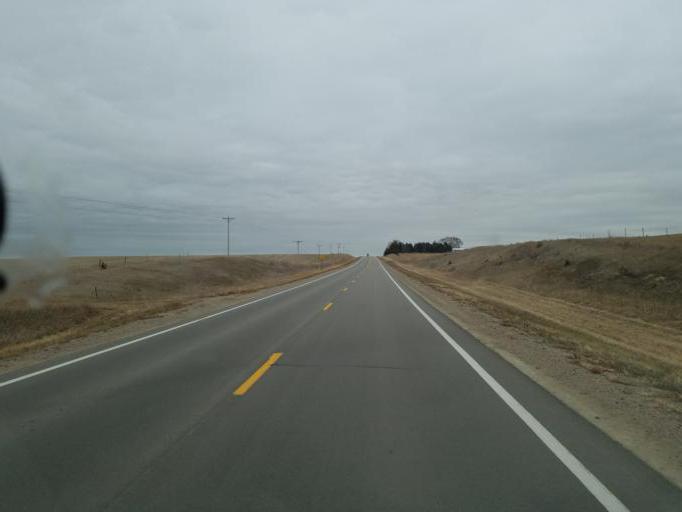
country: US
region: Nebraska
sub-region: Cedar County
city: Hartington
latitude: 42.6127
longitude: -97.3253
